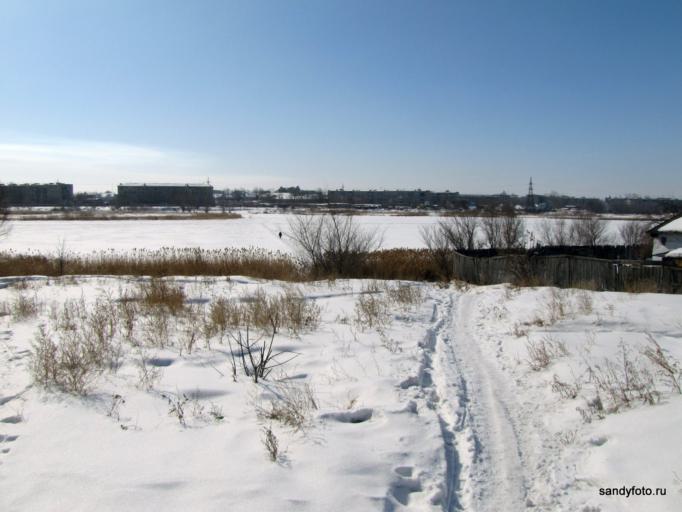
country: RU
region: Chelyabinsk
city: Troitsk
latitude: 54.0954
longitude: 61.5609
